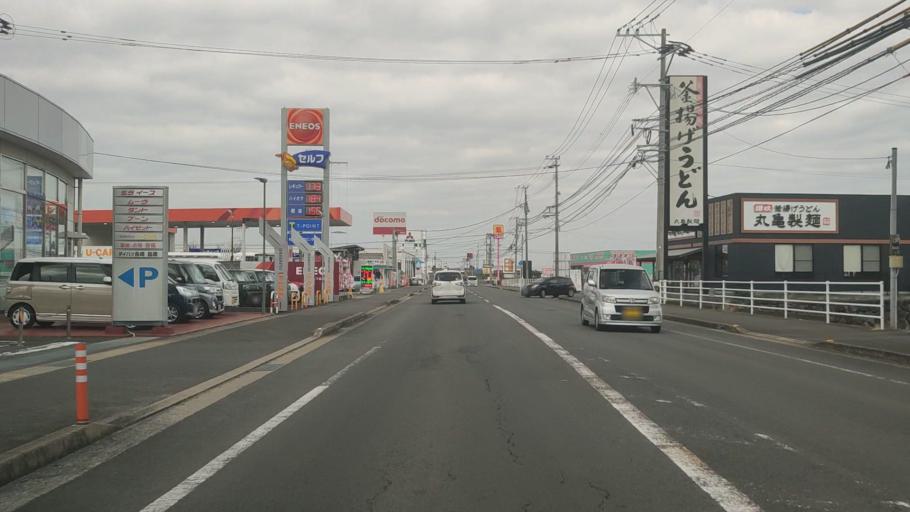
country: JP
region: Nagasaki
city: Shimabara
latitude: 32.8049
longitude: 130.3624
